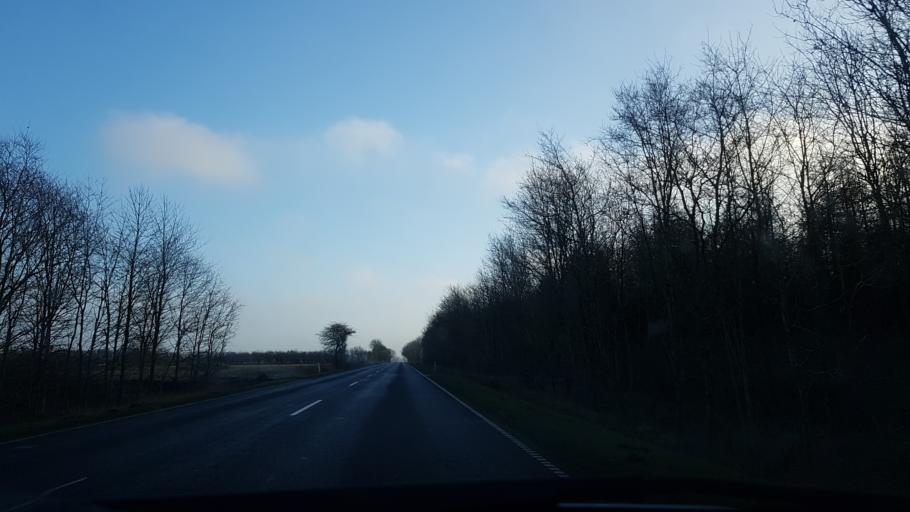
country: DK
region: South Denmark
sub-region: Haderslev Kommune
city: Vojens
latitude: 55.1806
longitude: 9.2352
